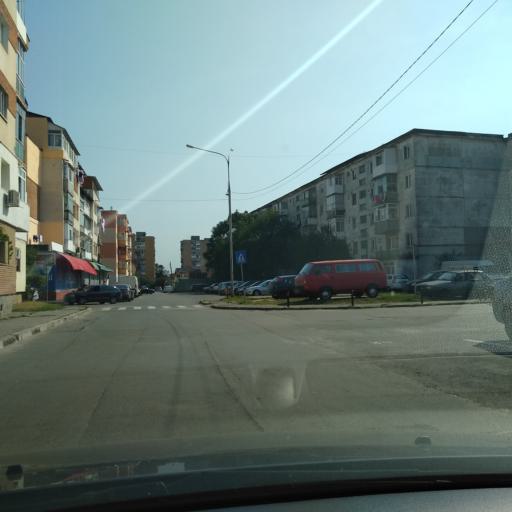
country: RO
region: Gorj
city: Targu Jiu
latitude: 45.0267
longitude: 23.2811
